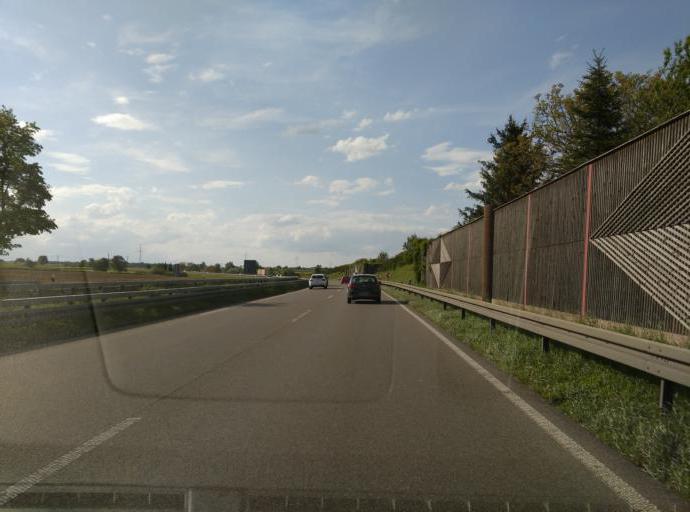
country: DE
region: Baden-Wuerttemberg
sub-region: Tuebingen Region
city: Kusterdingen
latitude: 48.5011
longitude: 9.1234
